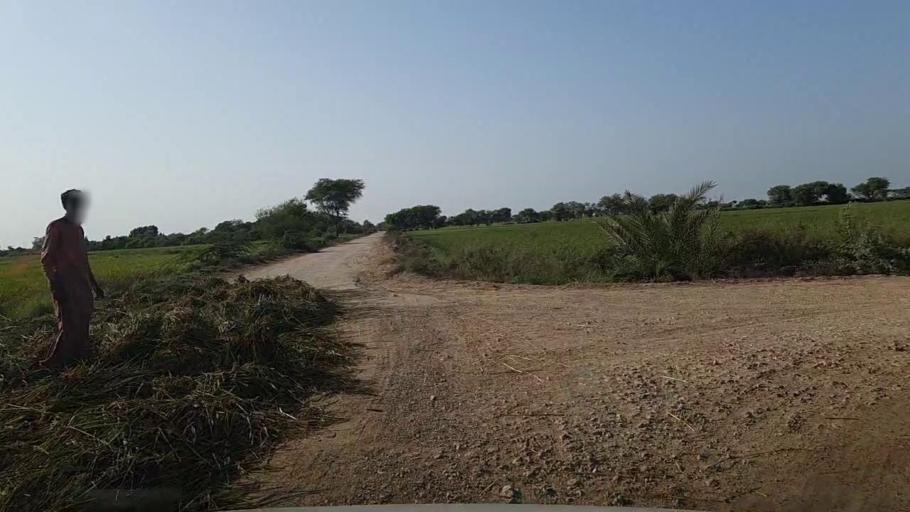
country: PK
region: Sindh
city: Kario
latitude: 24.8165
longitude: 68.4991
